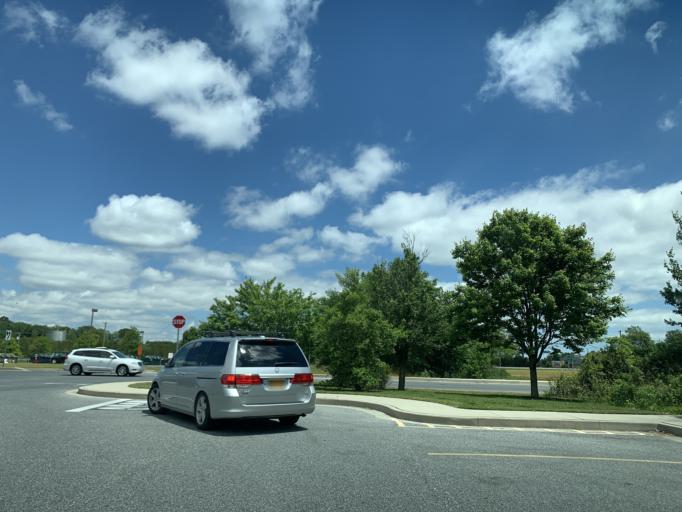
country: US
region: Maryland
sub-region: Worcester County
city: Ocean Pines
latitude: 38.3413
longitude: -75.1606
